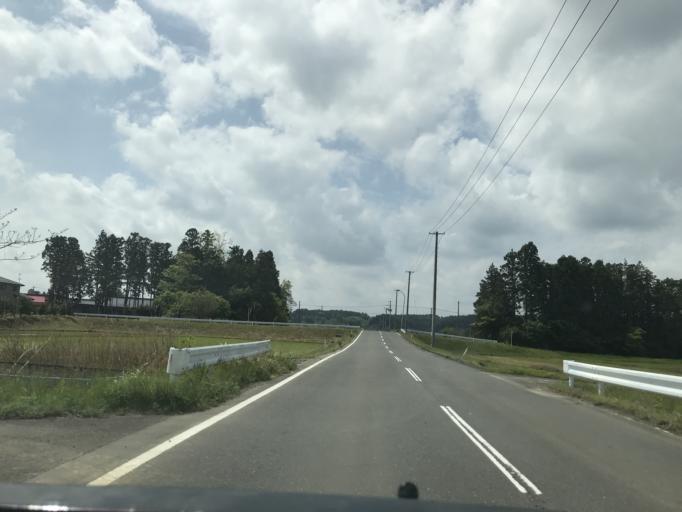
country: JP
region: Miyagi
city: Furukawa
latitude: 38.7504
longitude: 140.9356
